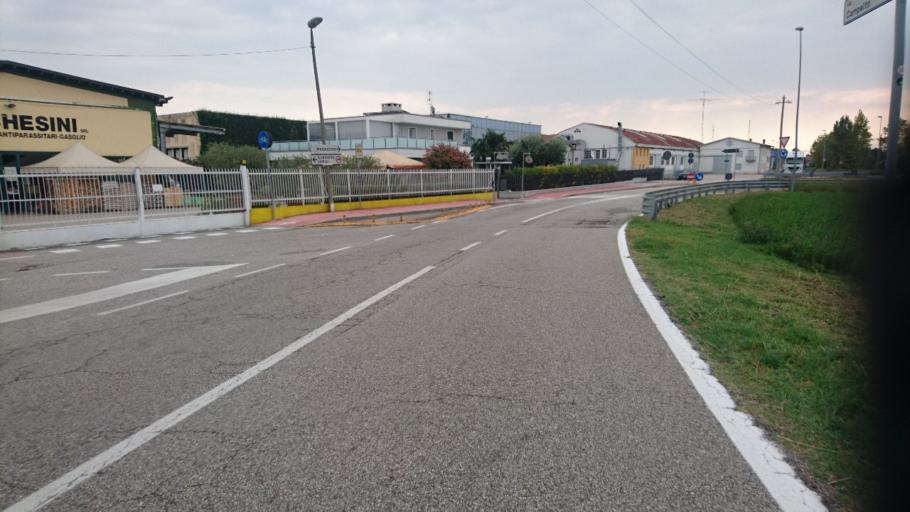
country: IT
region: Veneto
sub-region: Provincia di Verona
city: San Martino Buon Albergo
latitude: 45.4073
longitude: 11.0839
